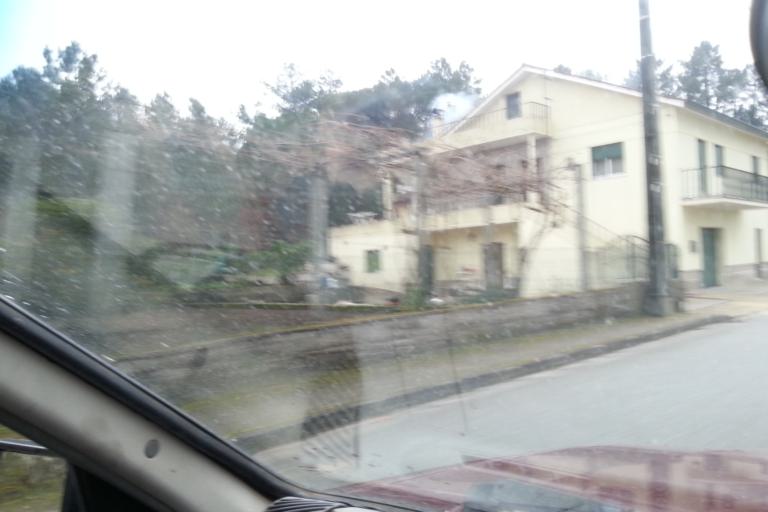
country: PT
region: Viseu
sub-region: Mangualde
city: Mangualde
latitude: 40.6166
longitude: -7.8006
